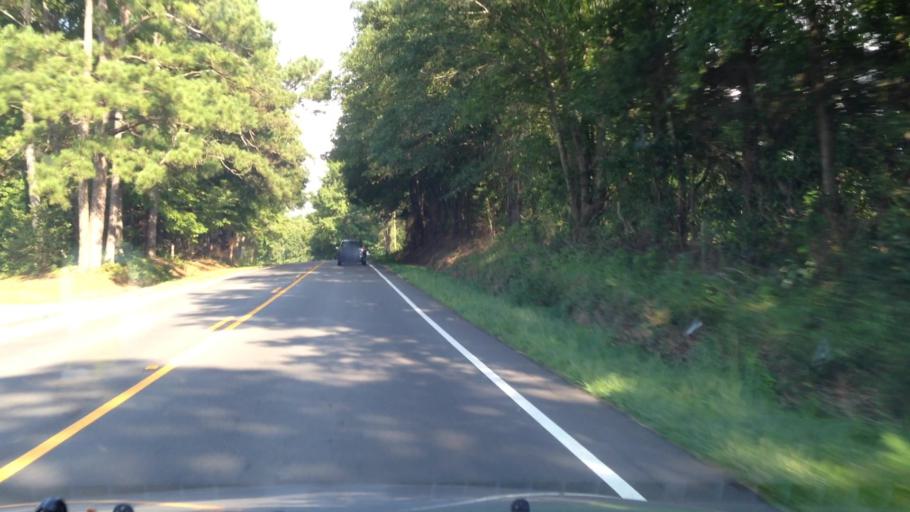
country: US
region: North Carolina
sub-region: Harnett County
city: Coats
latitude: 35.4124
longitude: -78.6904
